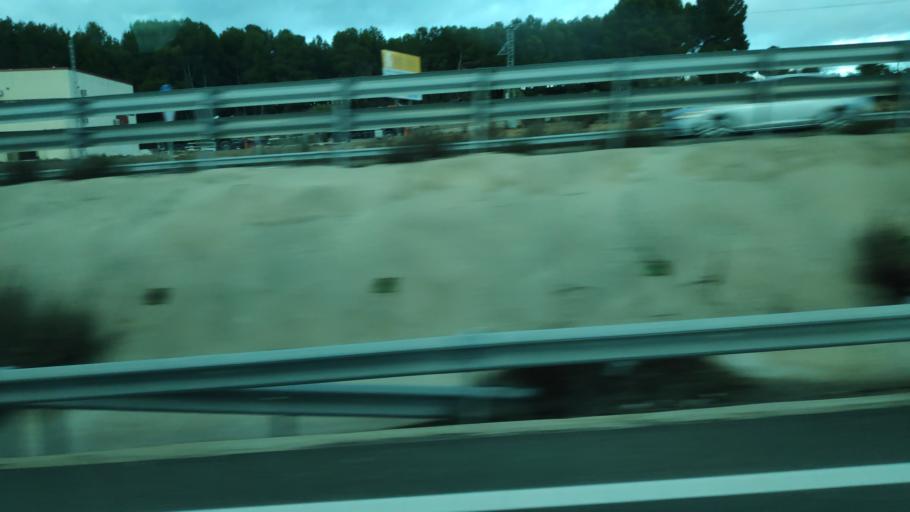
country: ES
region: Castille-La Mancha
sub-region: Provincia de Cuenca
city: Tarancon
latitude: 40.0156
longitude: -3.0319
